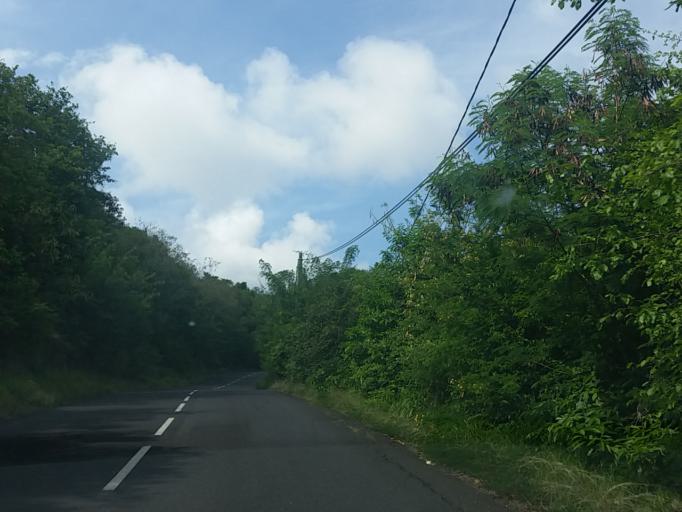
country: MQ
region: Martinique
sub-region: Martinique
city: Le Marin
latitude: 14.4236
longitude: -60.8756
